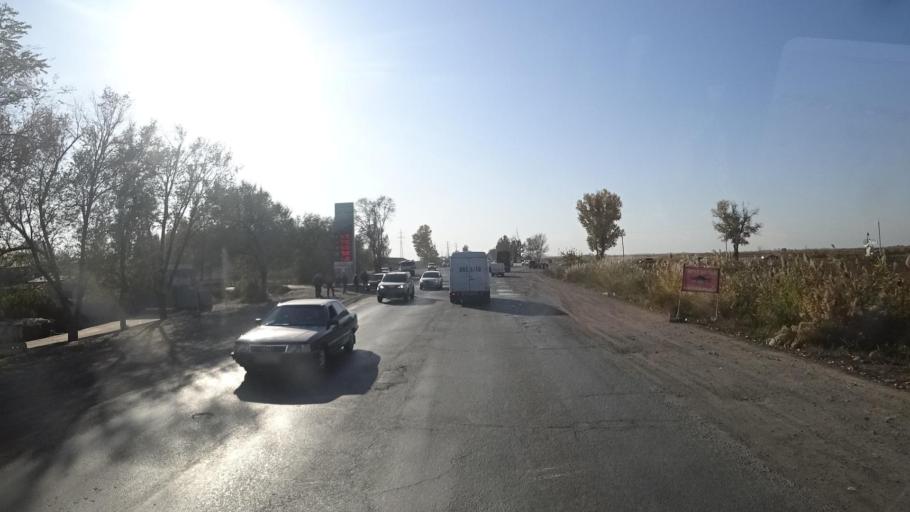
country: KG
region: Chuy
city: Bishkek
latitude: 42.9473
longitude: 74.5687
